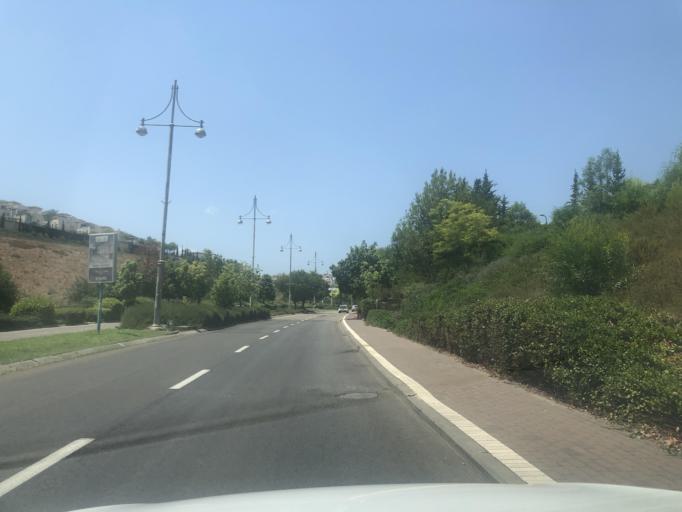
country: IL
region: Haifa
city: Daliyat el Karmil
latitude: 32.6487
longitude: 35.0982
